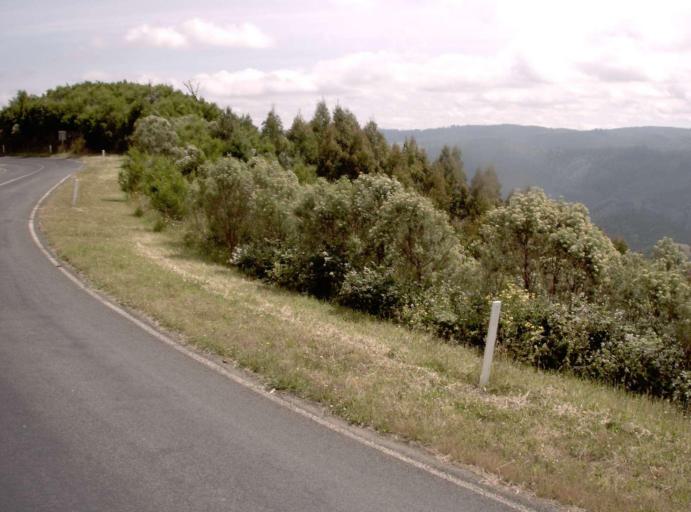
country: AU
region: Victoria
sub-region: Latrobe
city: Traralgon
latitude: -38.3652
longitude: 146.5658
